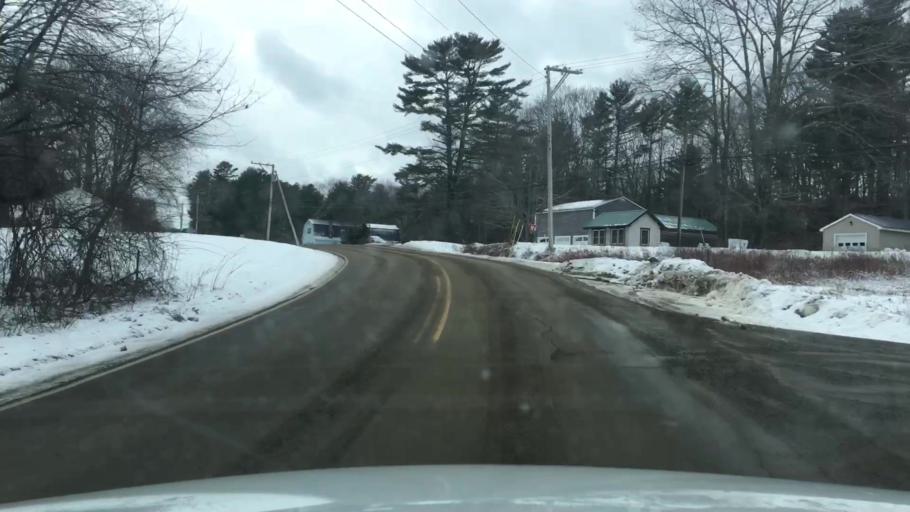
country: US
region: Maine
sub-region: Waldo County
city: Lincolnville
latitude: 44.2882
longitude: -69.0297
